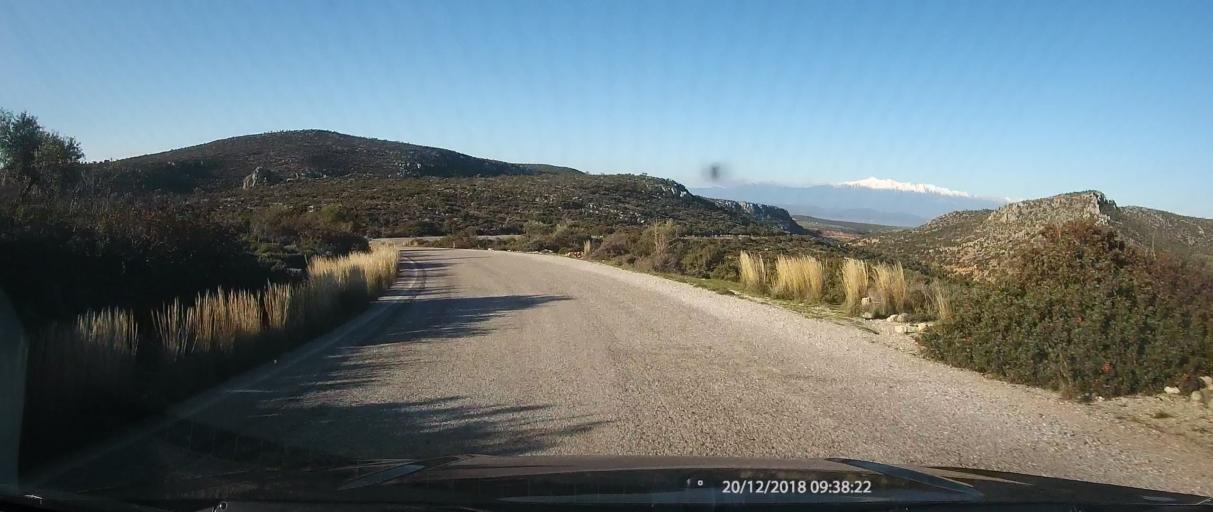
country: GR
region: Peloponnese
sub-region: Nomos Lakonias
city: Kato Glikovrisi
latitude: 36.9398
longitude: 22.7920
